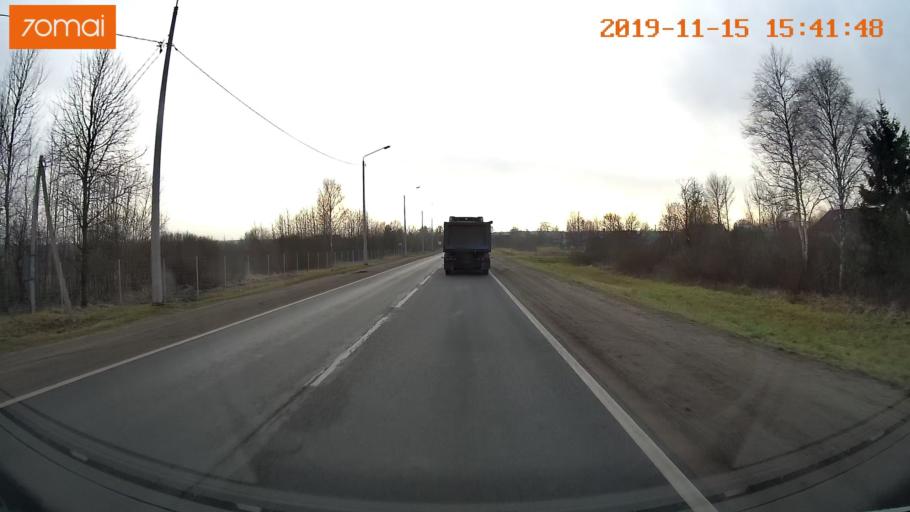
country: RU
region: Jaroslavl
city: Danilov
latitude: 57.9974
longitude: 40.0444
